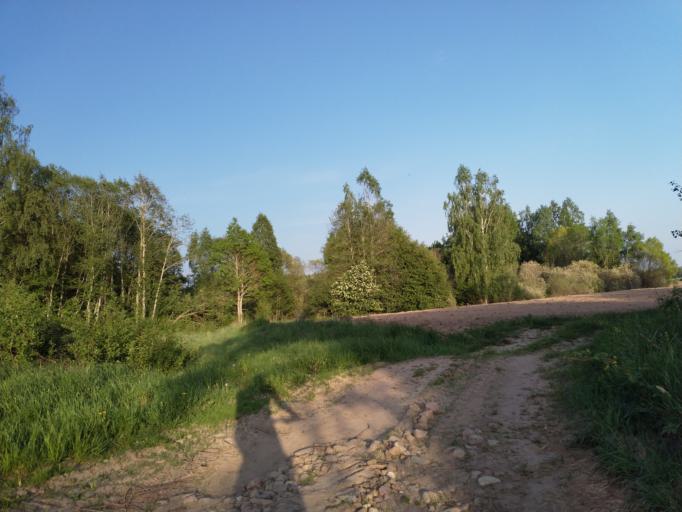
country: LV
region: Aizpute
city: Aizpute
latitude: 56.8321
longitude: 21.7825
